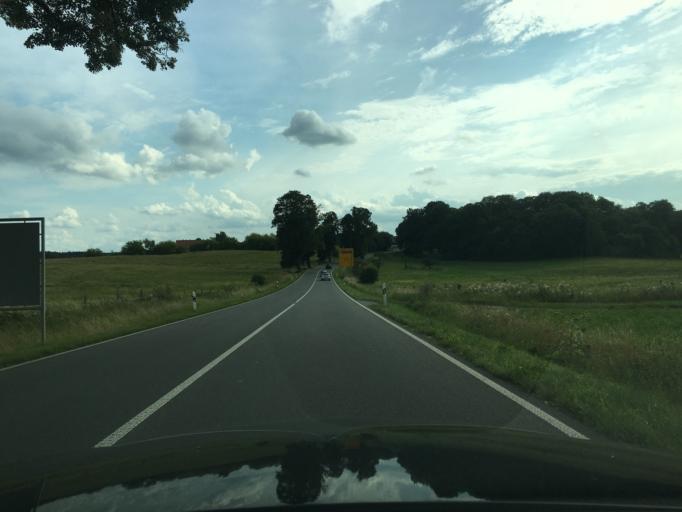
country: DE
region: Mecklenburg-Vorpommern
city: Penzlin
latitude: 53.4530
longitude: 13.0561
